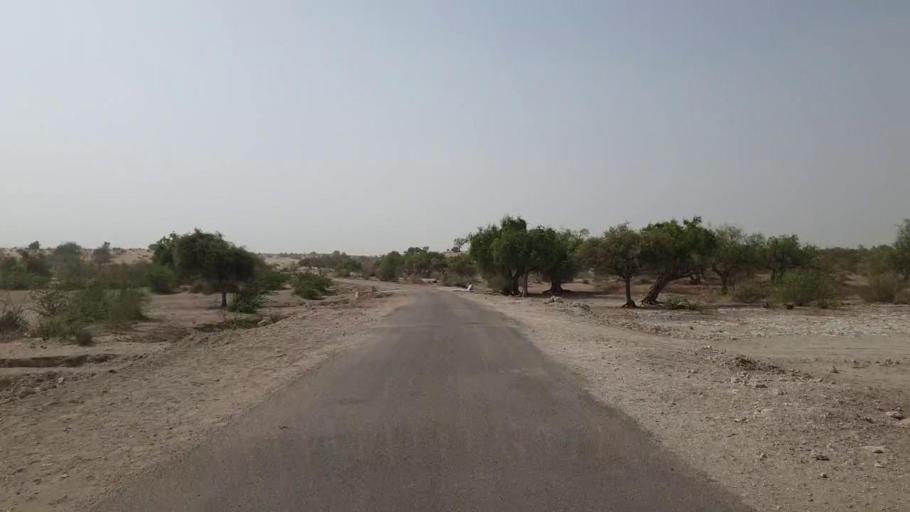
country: PK
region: Sindh
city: Mithi
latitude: 24.6170
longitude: 69.9188
